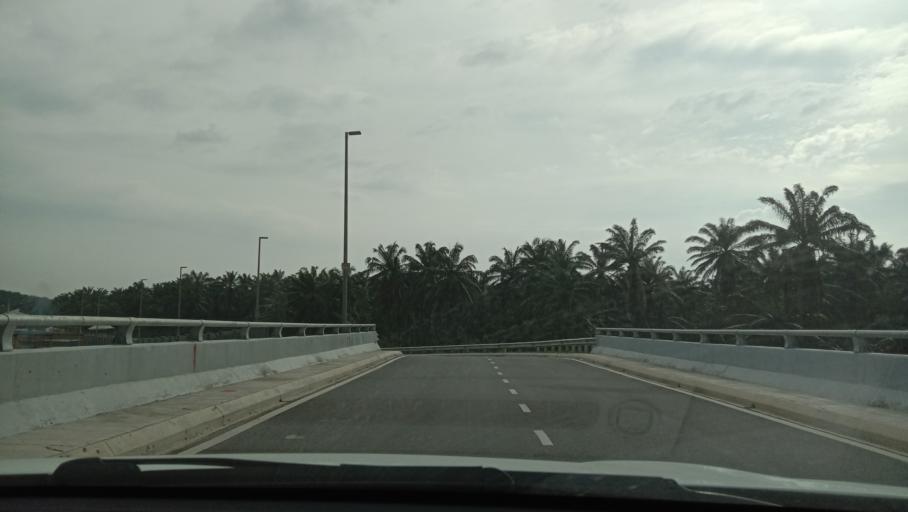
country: MY
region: Selangor
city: Ladang Seri Kundang
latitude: 3.2383
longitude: 101.4772
